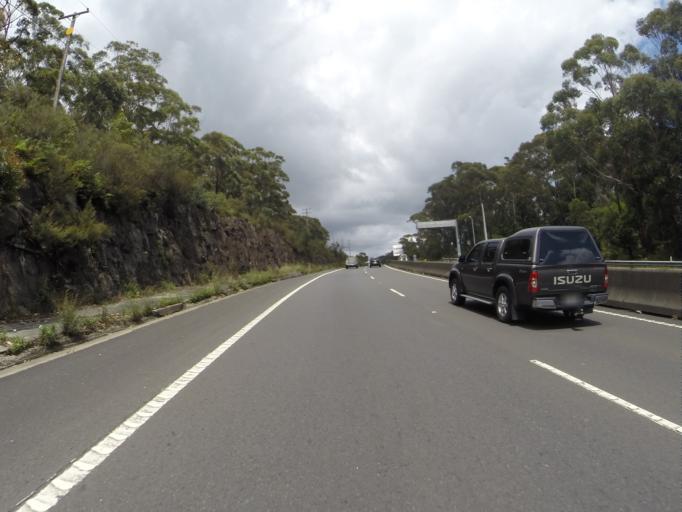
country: AU
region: New South Wales
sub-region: Wollongong
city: Bulli
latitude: -34.3215
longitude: 150.8871
